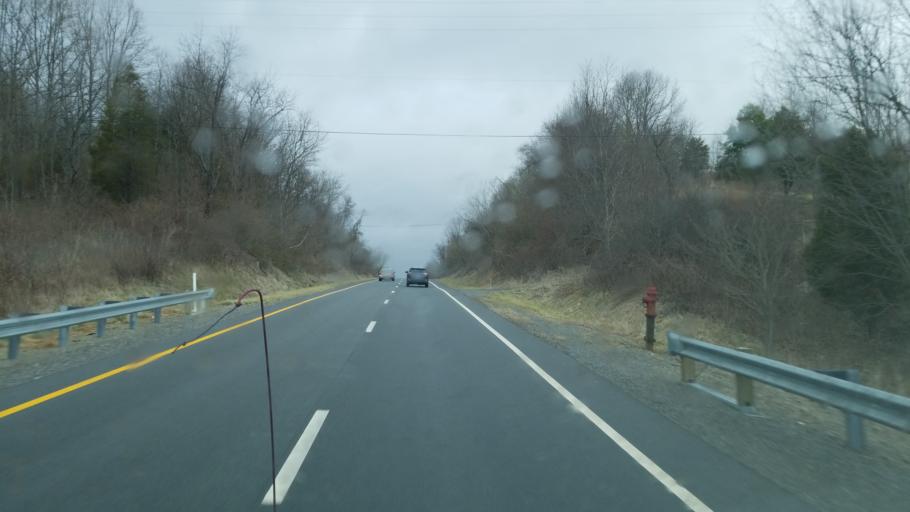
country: US
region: Virginia
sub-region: Giles County
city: Pearisburg
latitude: 37.2956
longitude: -80.7406
